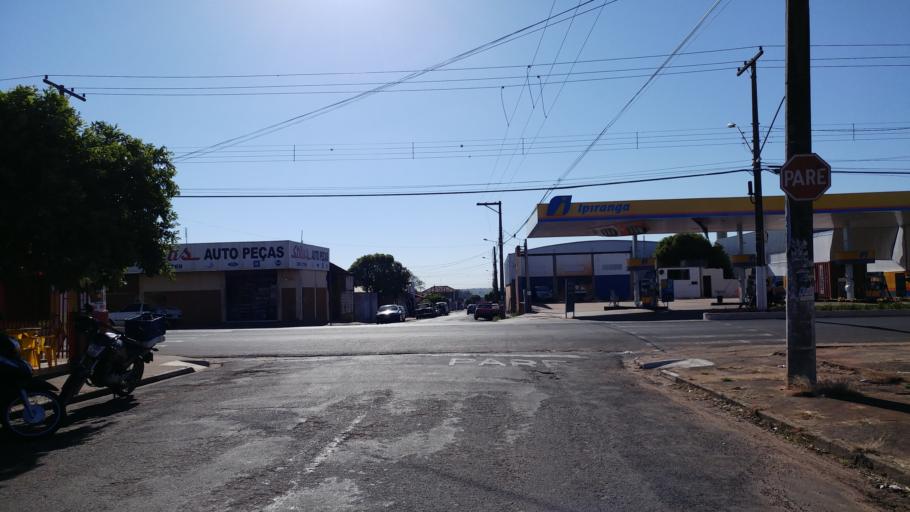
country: BR
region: Sao Paulo
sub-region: Paraguacu Paulista
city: Paraguacu Paulista
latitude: -22.4248
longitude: -50.5823
